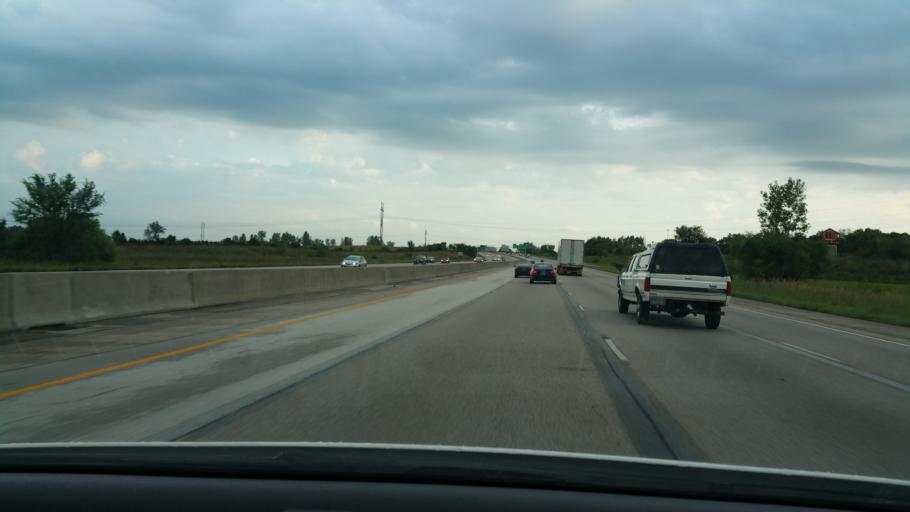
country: US
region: Iowa
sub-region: Polk County
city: Saylorville
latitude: 41.6787
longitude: -93.5772
